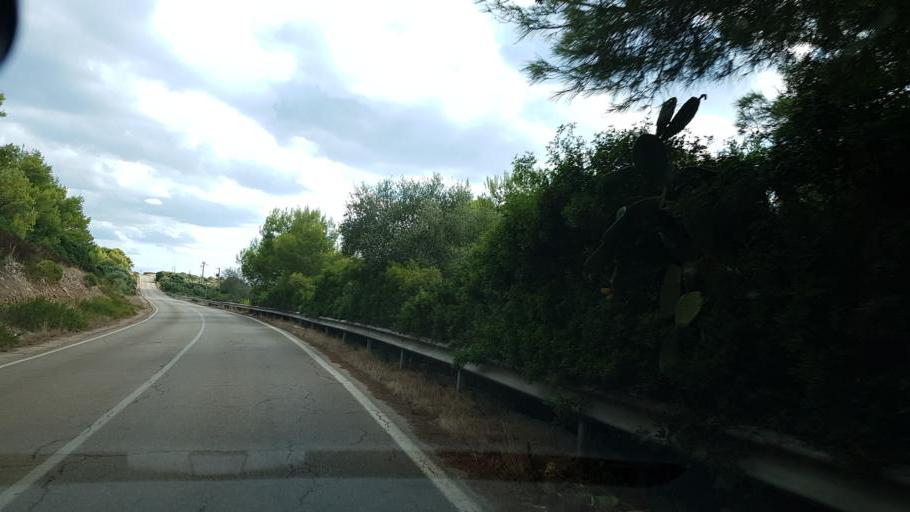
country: IT
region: Apulia
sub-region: Provincia di Lecce
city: Nardo
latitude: 40.1654
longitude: 17.9520
